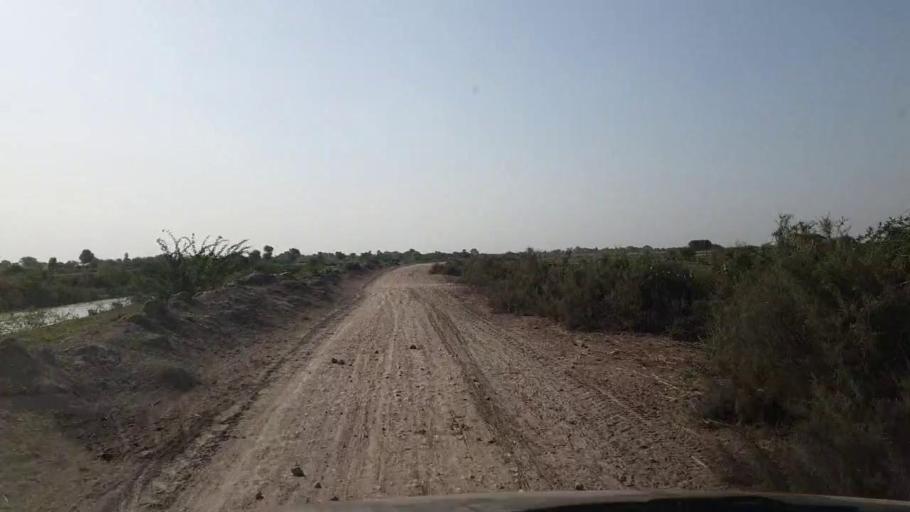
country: PK
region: Sindh
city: Kadhan
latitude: 24.6266
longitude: 69.0732
